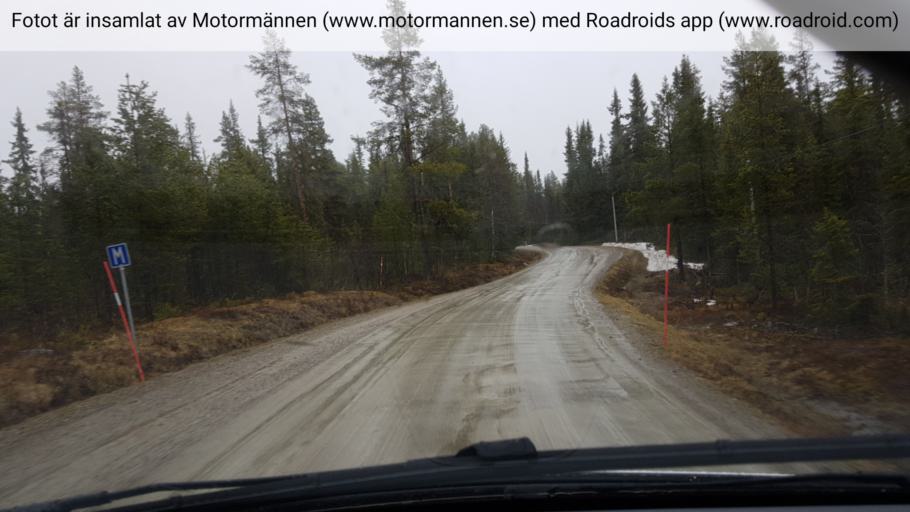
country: SE
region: Jaemtland
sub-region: Are Kommun
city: Are
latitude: 62.6229
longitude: 13.1849
